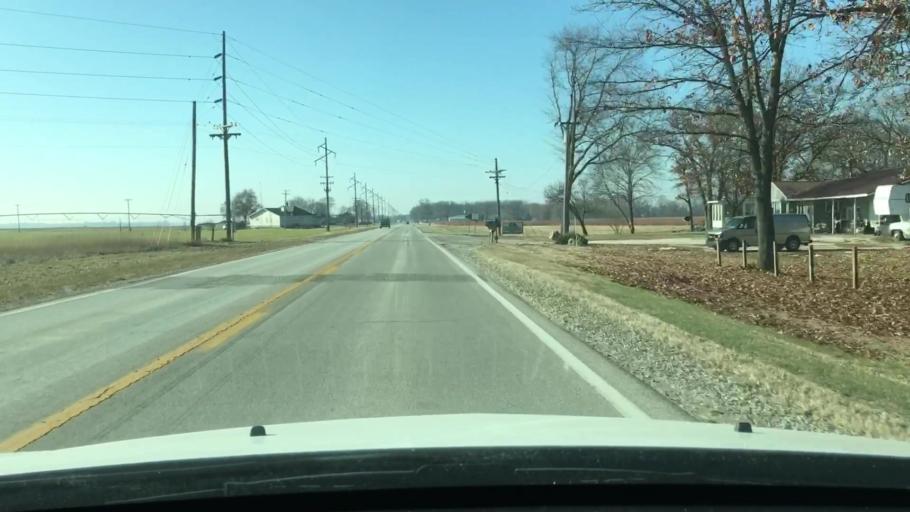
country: US
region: Illinois
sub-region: Cass County
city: Beardstown
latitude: 39.9888
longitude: -90.4403
